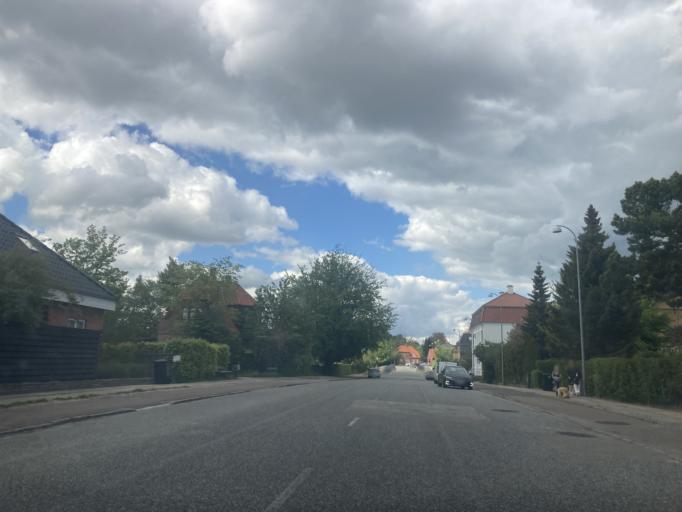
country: DK
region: Capital Region
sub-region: Gladsaxe Municipality
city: Buddinge
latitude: 55.7631
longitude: 12.4848
